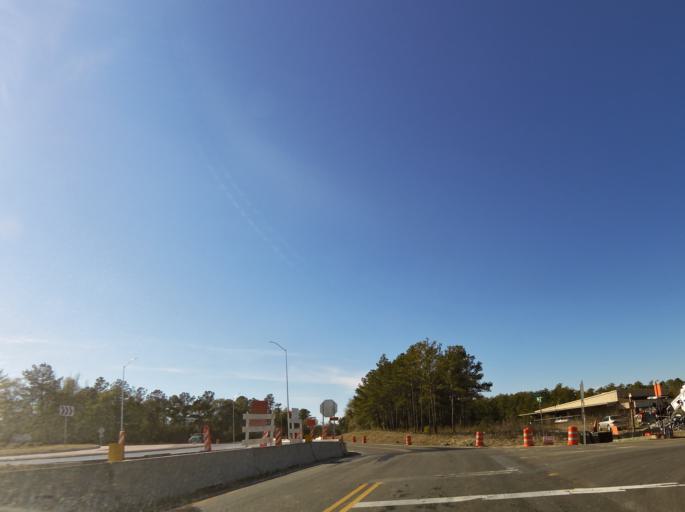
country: US
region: Georgia
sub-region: Bibb County
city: West Point
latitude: 32.8009
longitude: -83.8021
